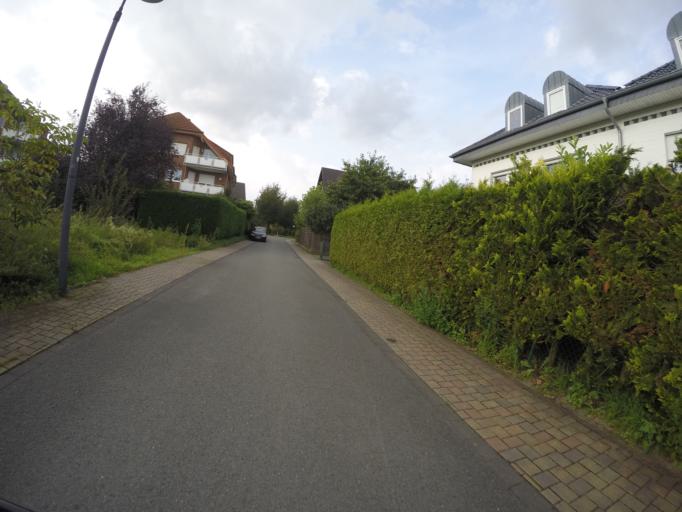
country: DE
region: North Rhine-Westphalia
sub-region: Regierungsbezirk Arnsberg
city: Lippstadt
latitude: 51.6816
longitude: 8.3257
